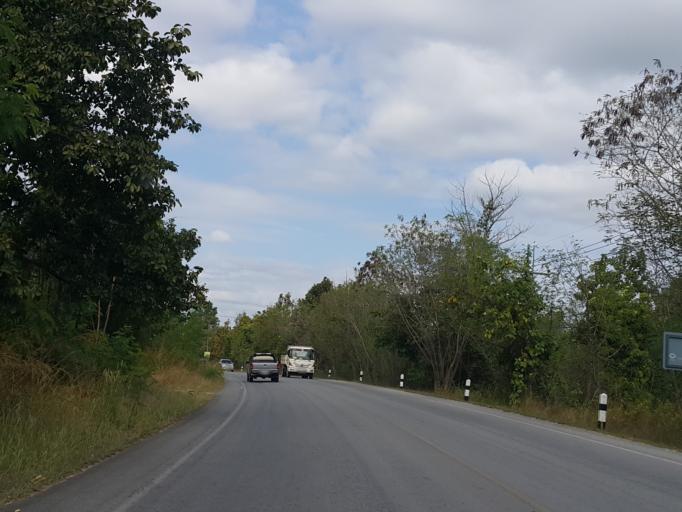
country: TH
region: Lampang
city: Lampang
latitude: 18.3890
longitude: 99.4597
